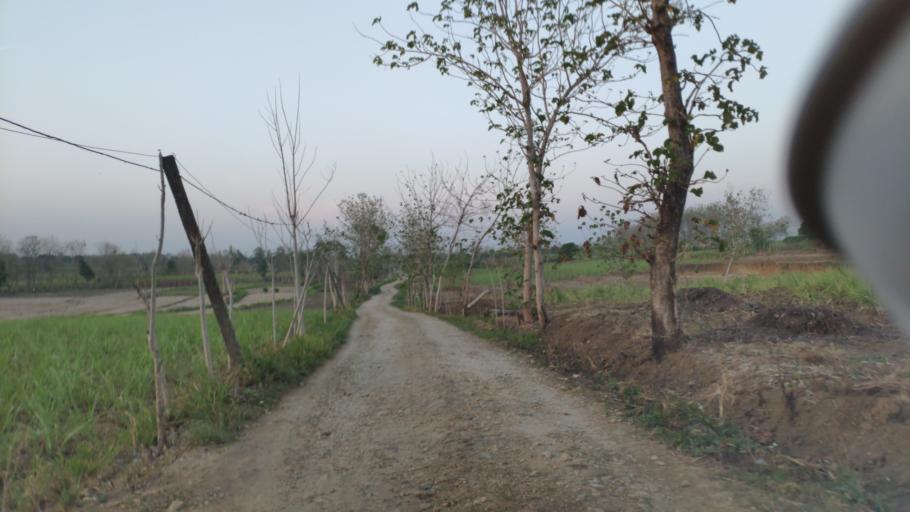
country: ID
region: Central Java
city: Jagong
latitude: -7.0415
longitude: 111.2388
